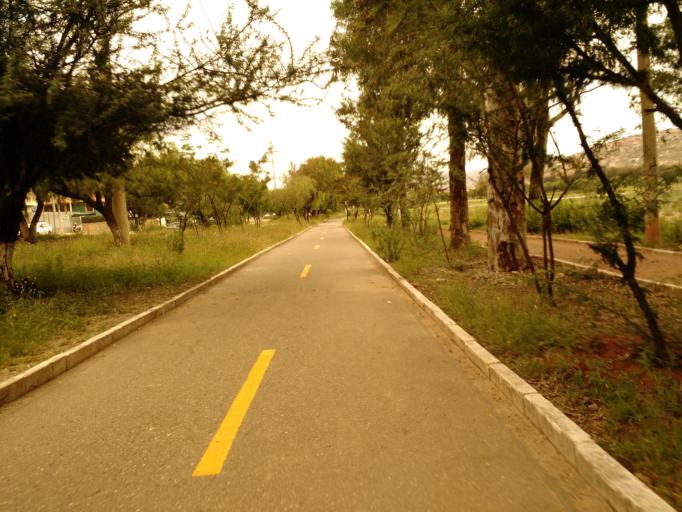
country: BO
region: Cochabamba
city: Cochabamba
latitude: -17.4110
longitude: -66.1268
